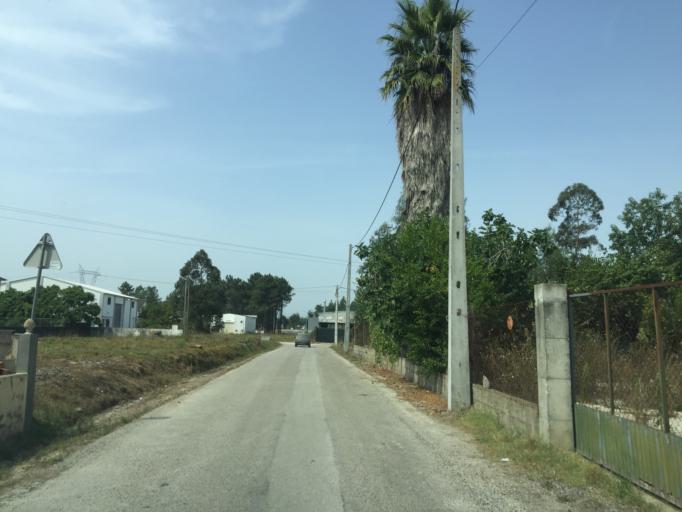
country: PT
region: Leiria
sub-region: Leiria
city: Amor
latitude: 39.7916
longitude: -8.8270
